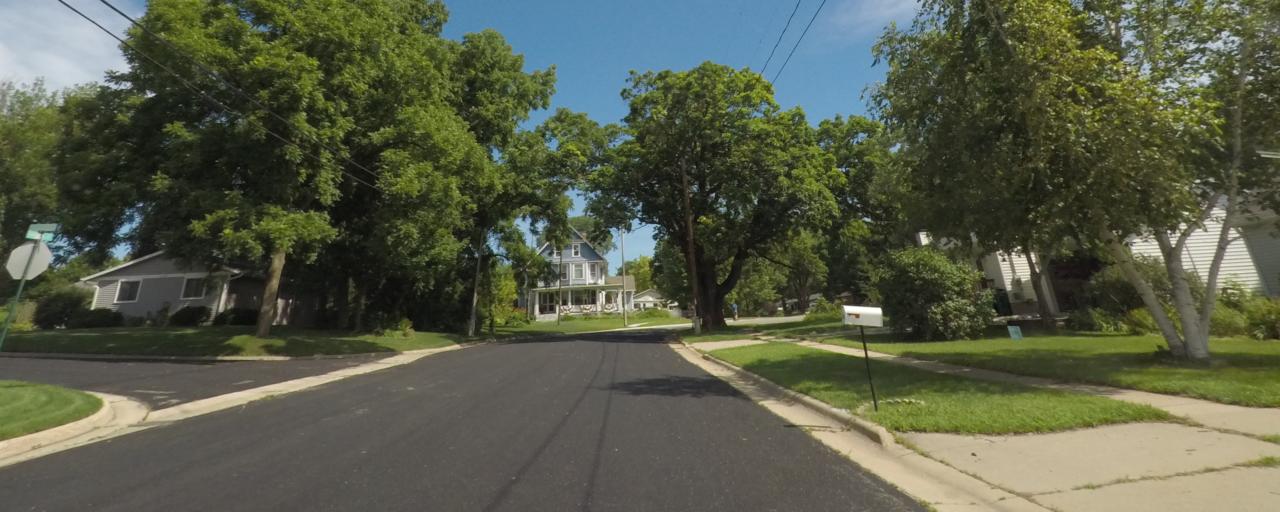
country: US
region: Wisconsin
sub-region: Dane County
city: McFarland
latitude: 43.0181
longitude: -89.2887
